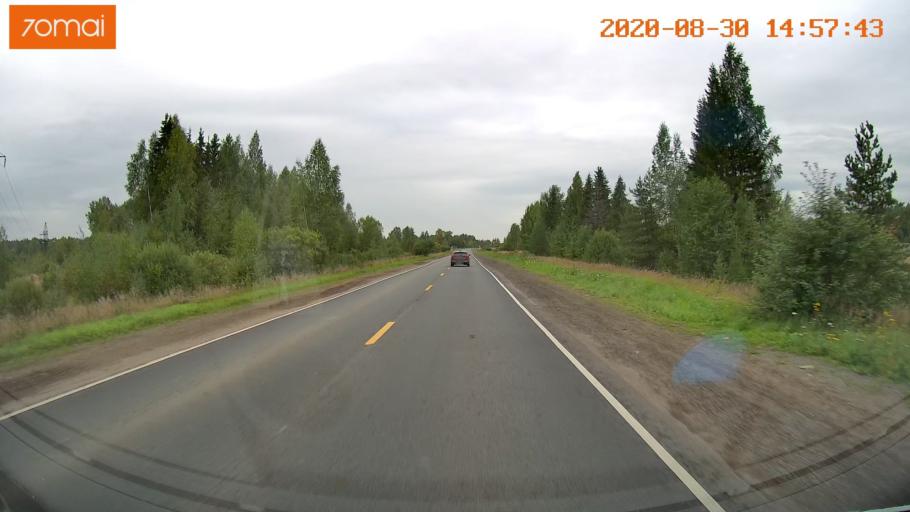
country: RU
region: Ivanovo
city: Navoloki
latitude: 57.3598
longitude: 42.0021
